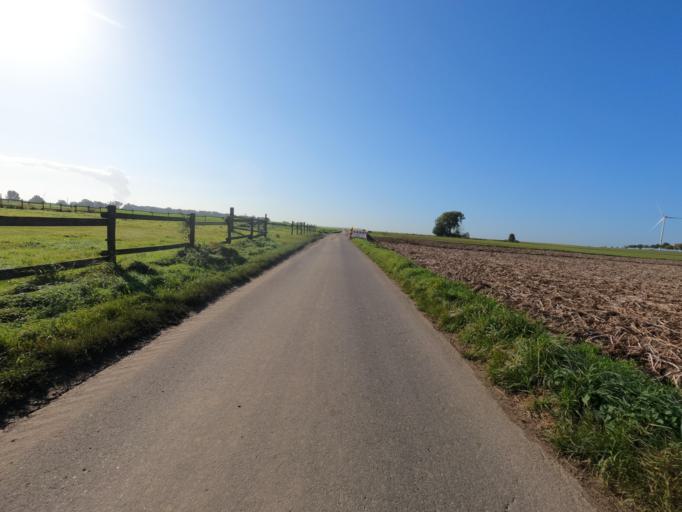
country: DE
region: North Rhine-Westphalia
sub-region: Regierungsbezirk Koln
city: Linnich
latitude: 50.9768
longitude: 6.2565
